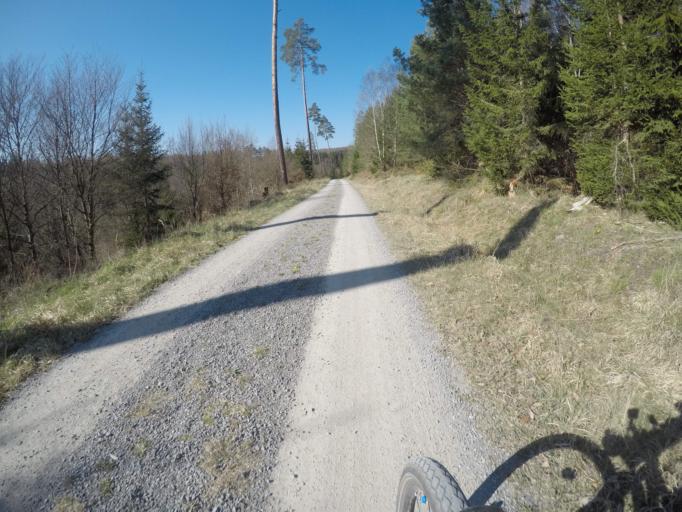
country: DE
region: Baden-Wuerttemberg
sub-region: Regierungsbezirk Stuttgart
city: Weil im Schonbuch
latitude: 48.5918
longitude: 9.0484
